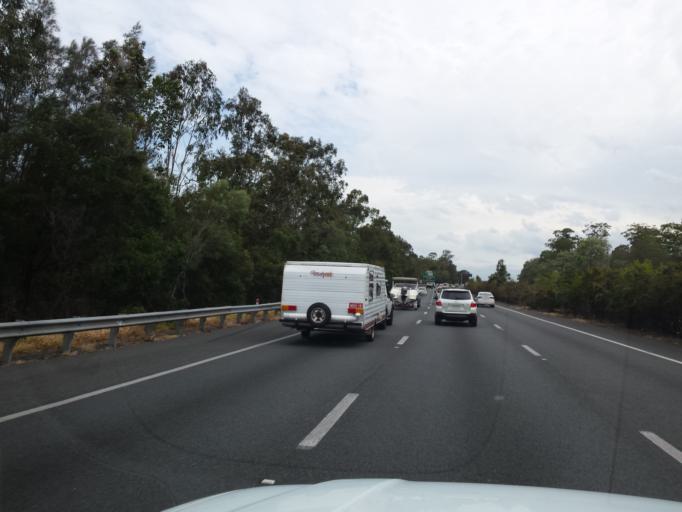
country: AU
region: Queensland
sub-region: Gold Coast
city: Nerang
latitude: -27.9649
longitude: 153.3461
